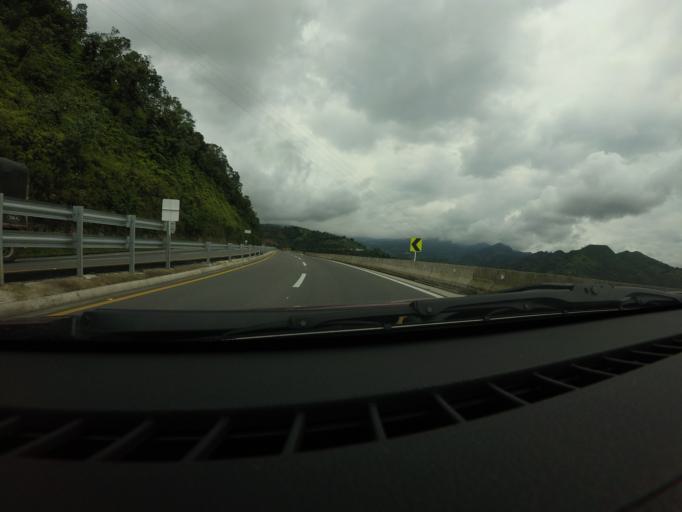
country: CO
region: Cundinamarca
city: La Vega
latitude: 4.9893
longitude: -74.3239
